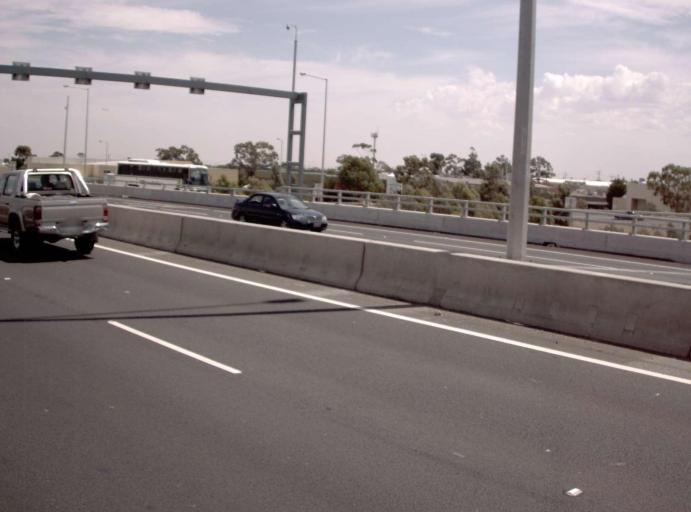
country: AU
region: Victoria
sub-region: Moreland
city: Gowanbrae
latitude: -37.7050
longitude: 144.8891
